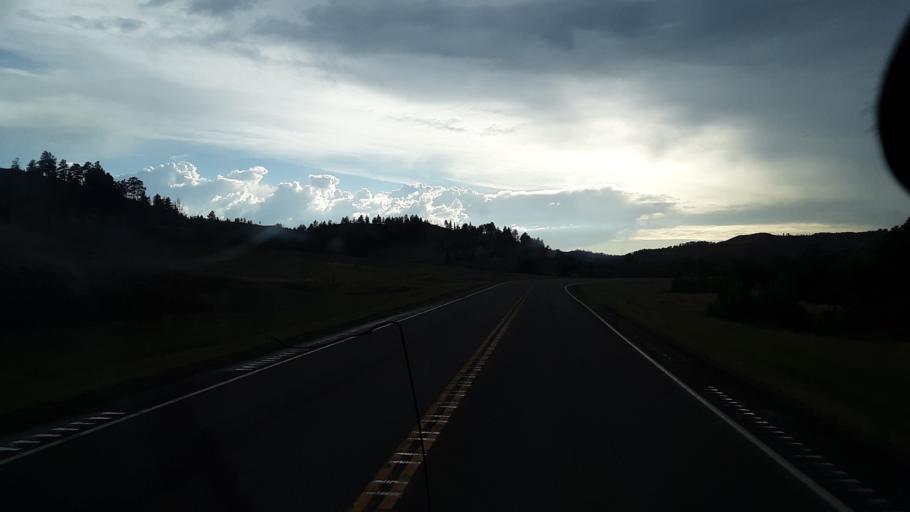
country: US
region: Montana
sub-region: Rosebud County
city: Lame Deer
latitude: 45.6188
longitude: -106.4064
